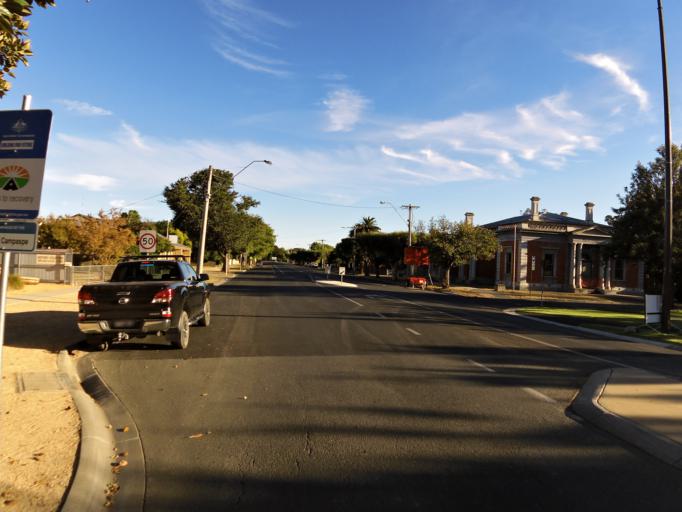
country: AU
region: New South Wales
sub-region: Murray Shire
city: Moama
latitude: -36.1195
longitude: 144.7455
